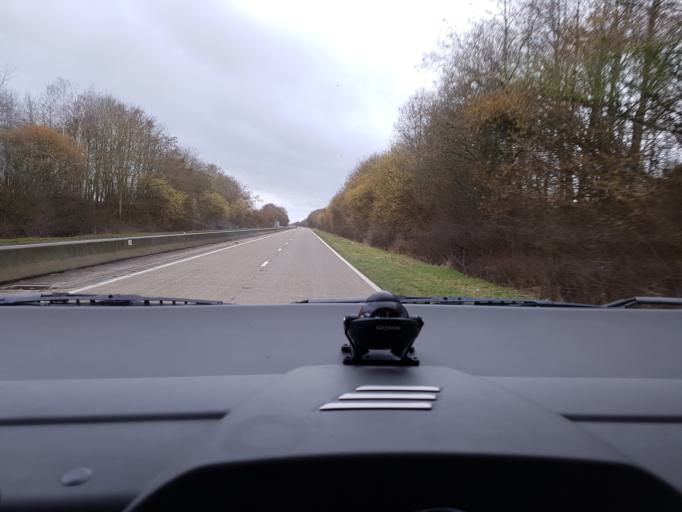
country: BE
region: Wallonia
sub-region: Province de Namur
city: Ciney
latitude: 50.2794
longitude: 5.0675
